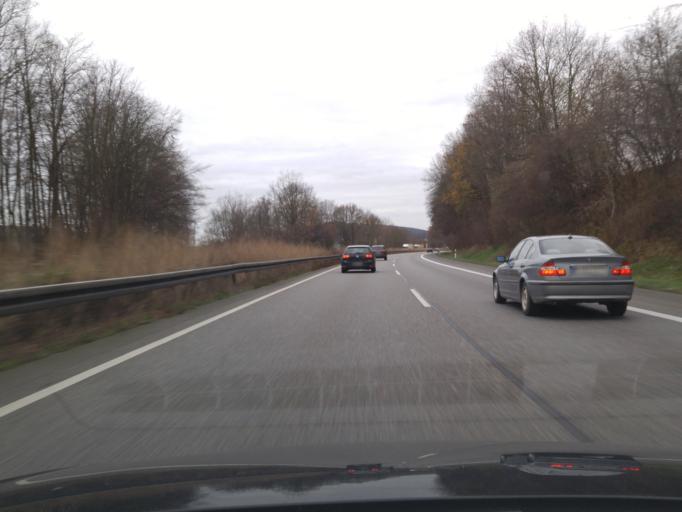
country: DE
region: Lower Saxony
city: Kalefeld
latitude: 51.7947
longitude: 10.0795
